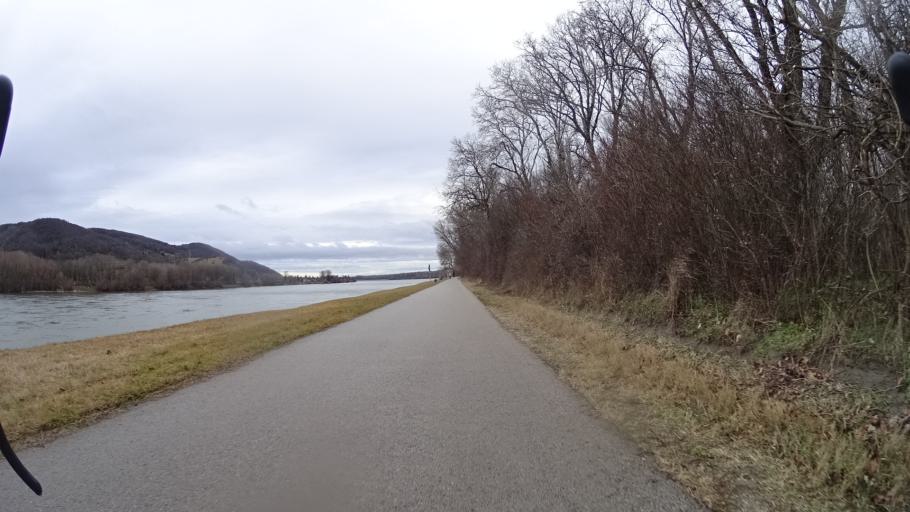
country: AT
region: Lower Austria
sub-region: Politischer Bezirk Korneuburg
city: Korneuburg
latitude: 48.3463
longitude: 16.3021
